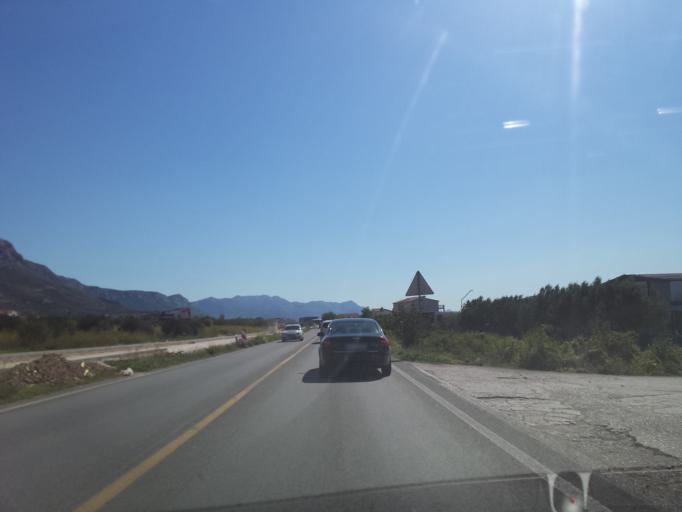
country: HR
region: Splitsko-Dalmatinska
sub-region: Grad Trogir
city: Trogir
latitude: 43.5588
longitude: 16.3453
